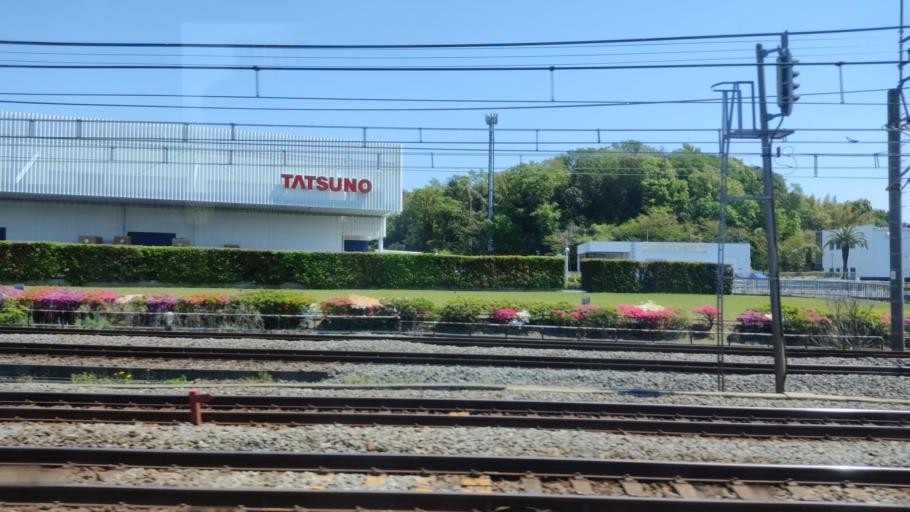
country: JP
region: Kanagawa
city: Kamakura
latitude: 35.3647
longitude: 139.5303
